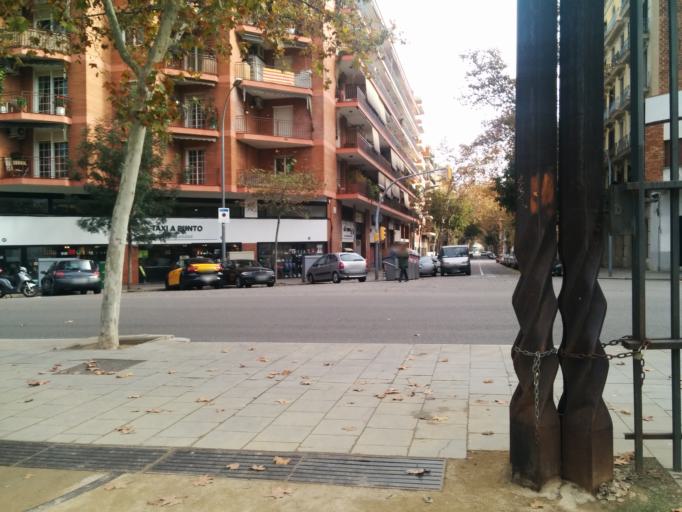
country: ES
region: Catalonia
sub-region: Provincia de Barcelona
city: Ciutat Vella
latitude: 41.3933
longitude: 2.1845
